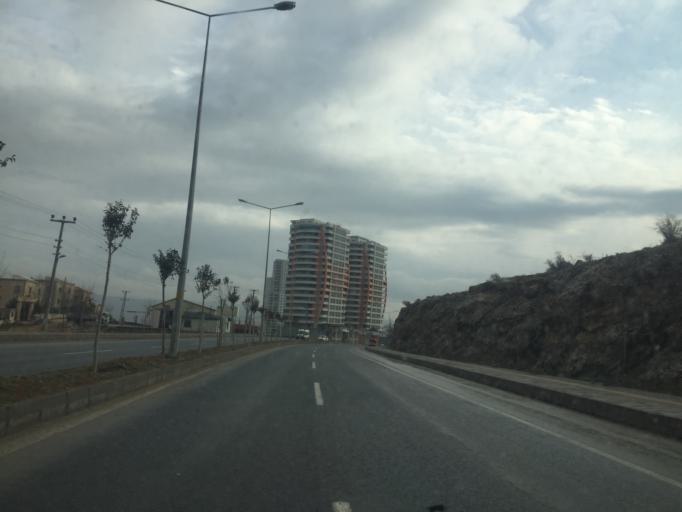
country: TR
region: Mardin
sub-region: Mardin Ilcesi
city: Mardin
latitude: 37.3220
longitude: 40.7325
